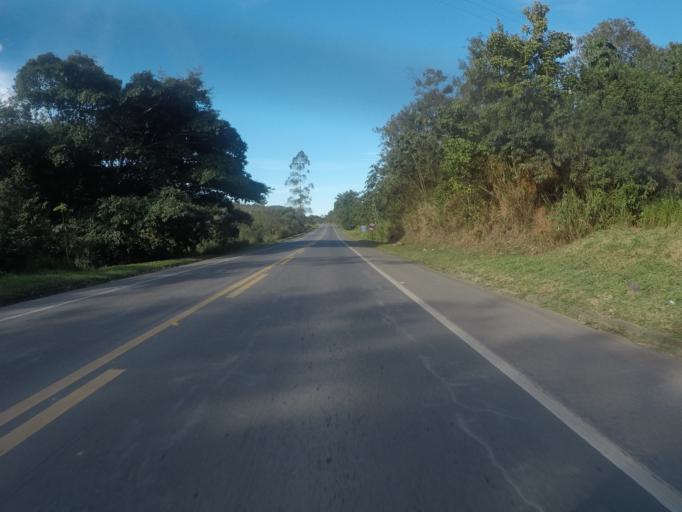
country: BR
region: Espirito Santo
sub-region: Ibiracu
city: Ibiracu
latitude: -19.8672
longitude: -40.4014
